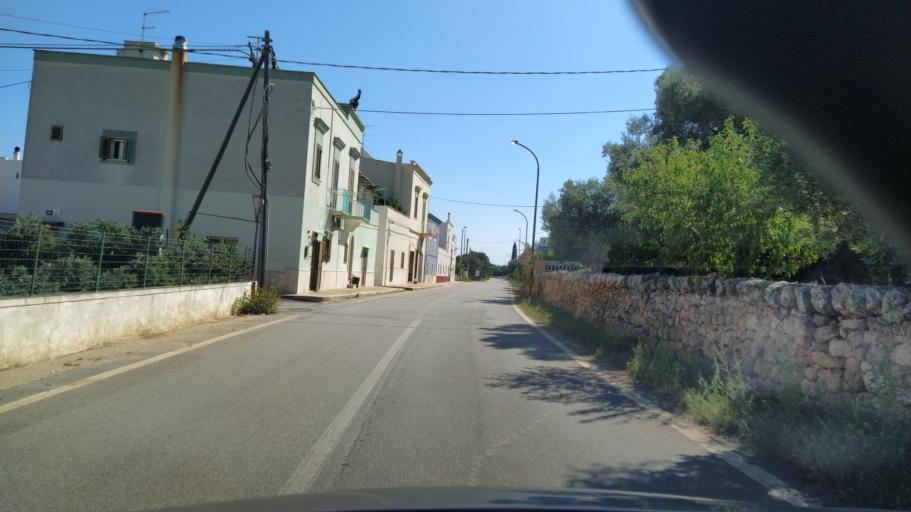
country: IT
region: Apulia
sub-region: Provincia di Brindisi
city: Fasano
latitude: 40.8967
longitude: 17.3529
